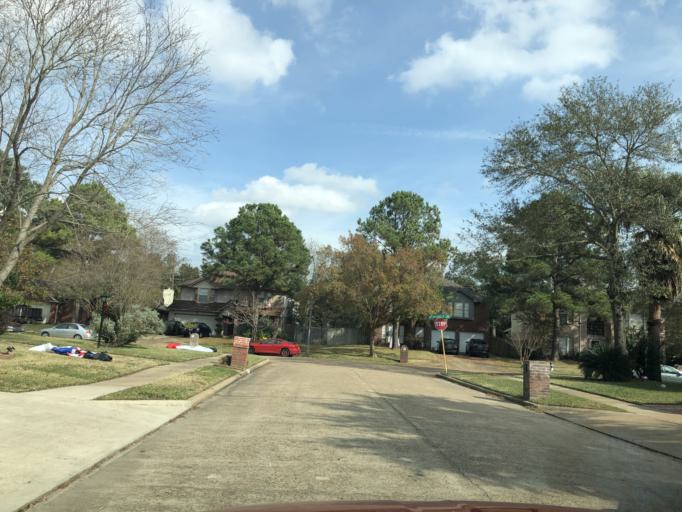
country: US
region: Texas
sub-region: Harris County
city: Tomball
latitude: 30.0403
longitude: -95.5437
